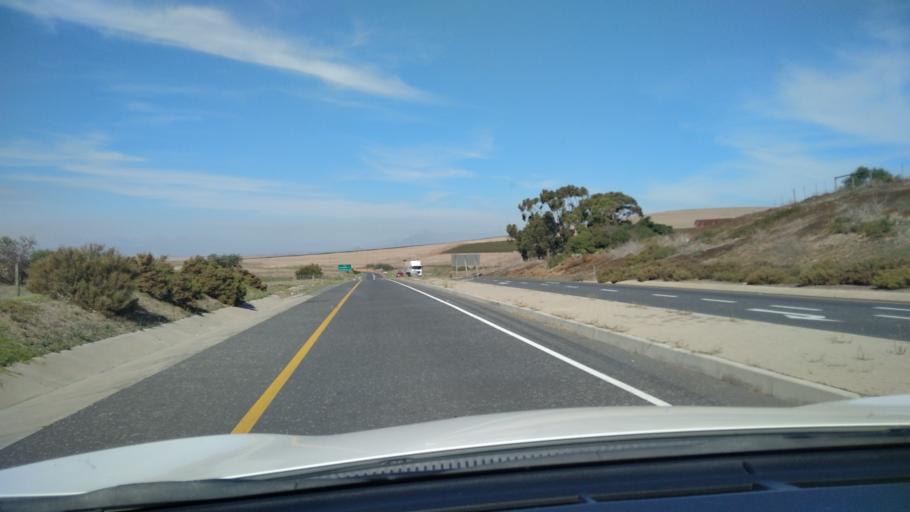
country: ZA
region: Western Cape
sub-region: City of Cape Town
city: Atlantis
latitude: -33.6638
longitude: 18.5613
